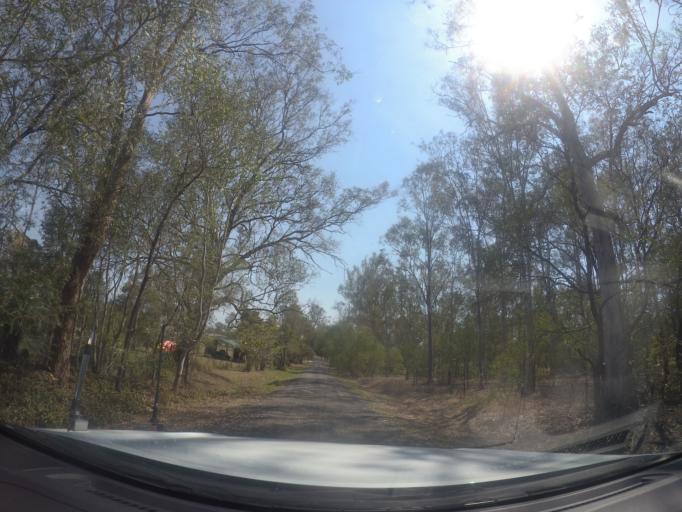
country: AU
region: Queensland
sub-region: Logan
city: North Maclean
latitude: -27.7893
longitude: 153.0274
